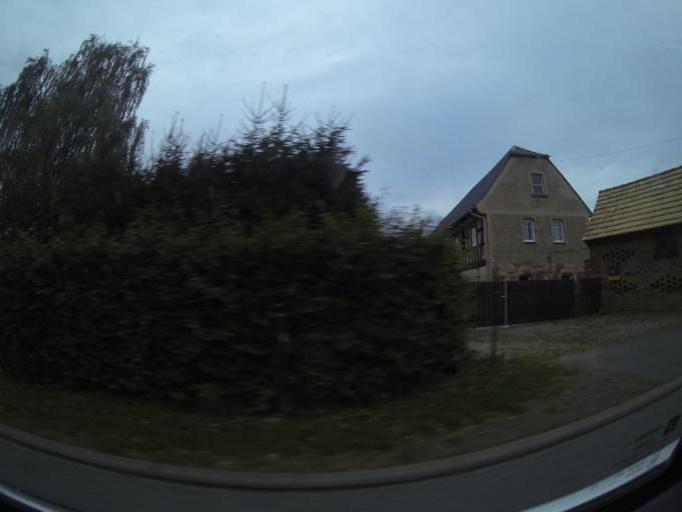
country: DE
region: Thuringia
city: Wildenborten
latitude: 50.8942
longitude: 12.2970
